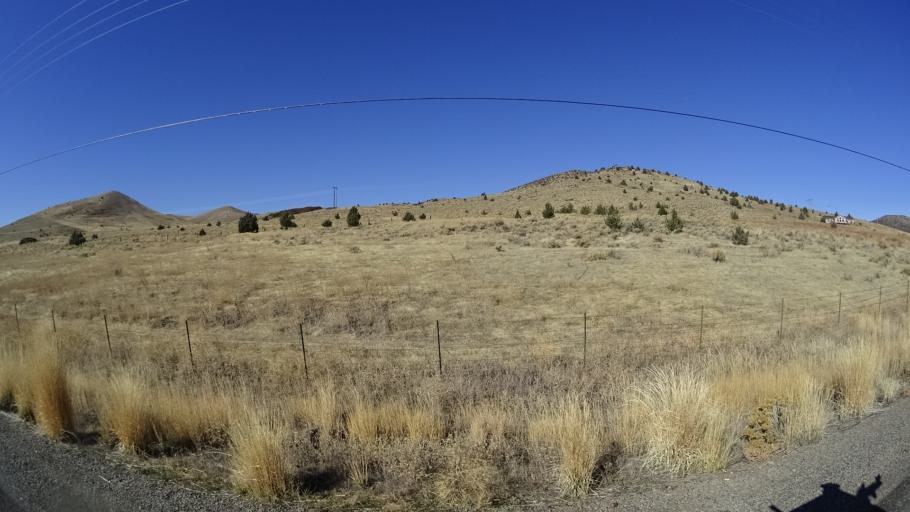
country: US
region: California
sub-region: Siskiyou County
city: Montague
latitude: 41.7873
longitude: -122.5168
